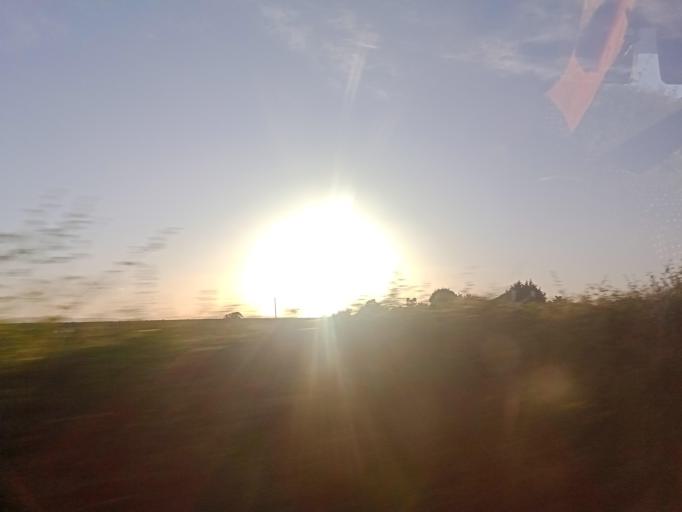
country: IE
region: Leinster
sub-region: Kilkenny
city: Castlecomer
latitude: 52.7329
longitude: -7.2366
